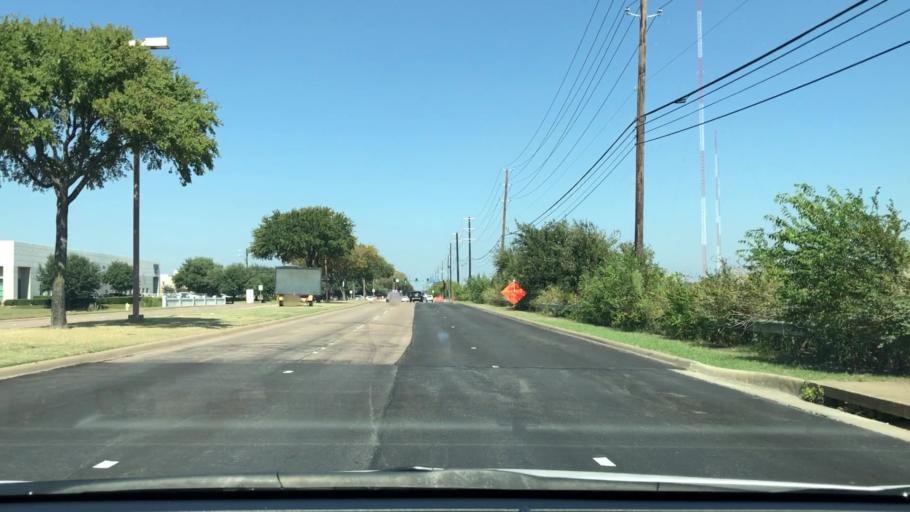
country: US
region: Texas
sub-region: Dallas County
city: Coppell
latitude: 32.9379
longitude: -96.9935
